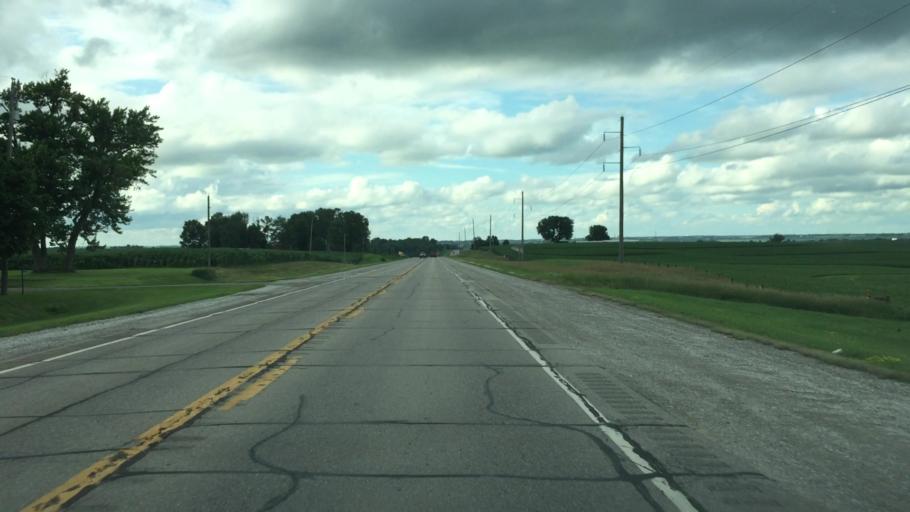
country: US
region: Iowa
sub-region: Jasper County
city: Monroe
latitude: 41.5751
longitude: -93.0970
